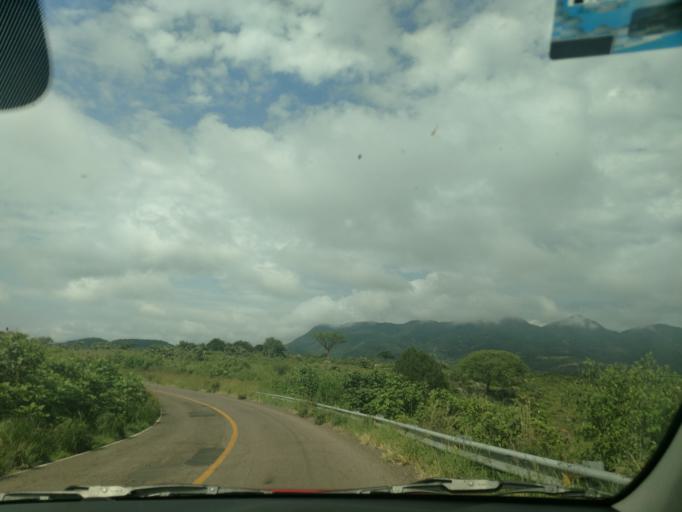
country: MX
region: Jalisco
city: El Salto
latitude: 20.3860
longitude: -104.5343
